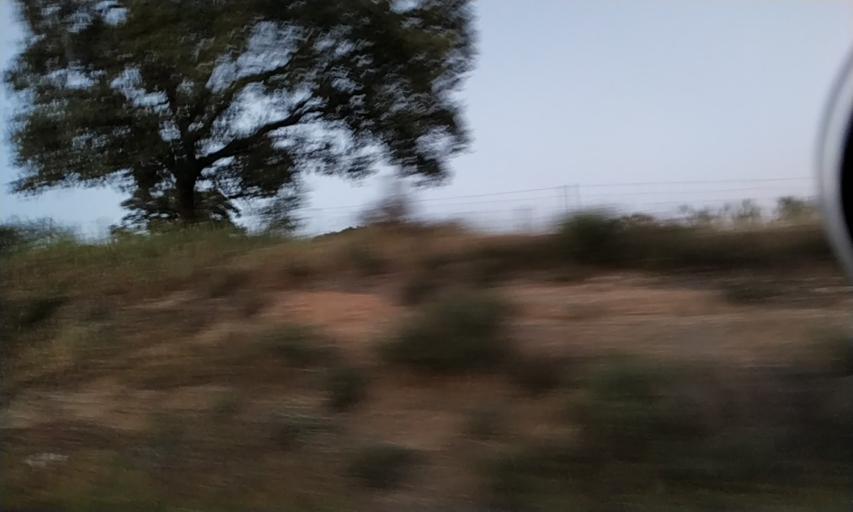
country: ES
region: Extremadura
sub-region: Provincia de Caceres
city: Alcantara
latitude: 39.7510
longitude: -6.9031
